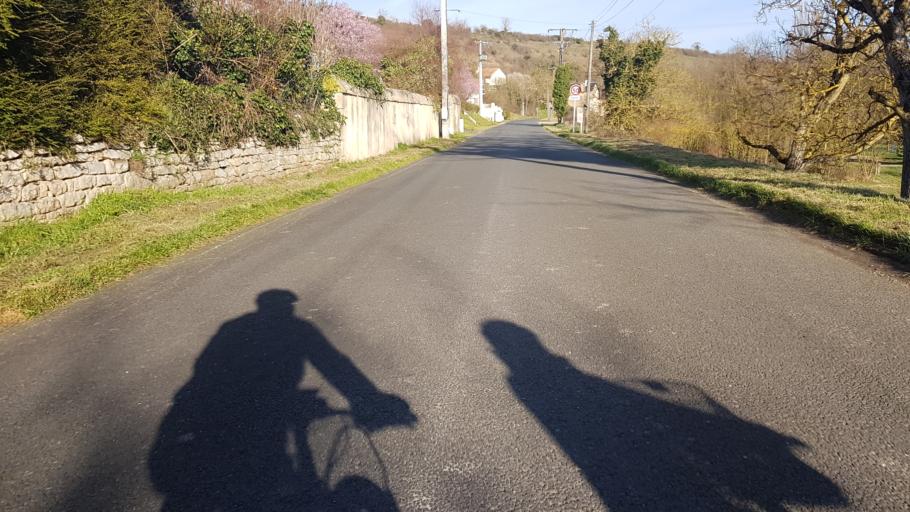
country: FR
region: Poitou-Charentes
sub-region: Departement de la Vienne
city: Migne-Auxances
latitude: 46.6422
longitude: 0.3398
